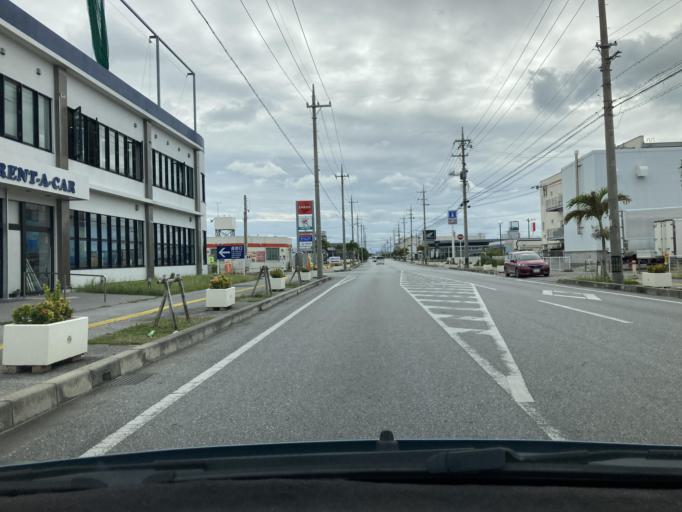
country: JP
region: Okinawa
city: Itoman
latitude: 26.1590
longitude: 127.6542
